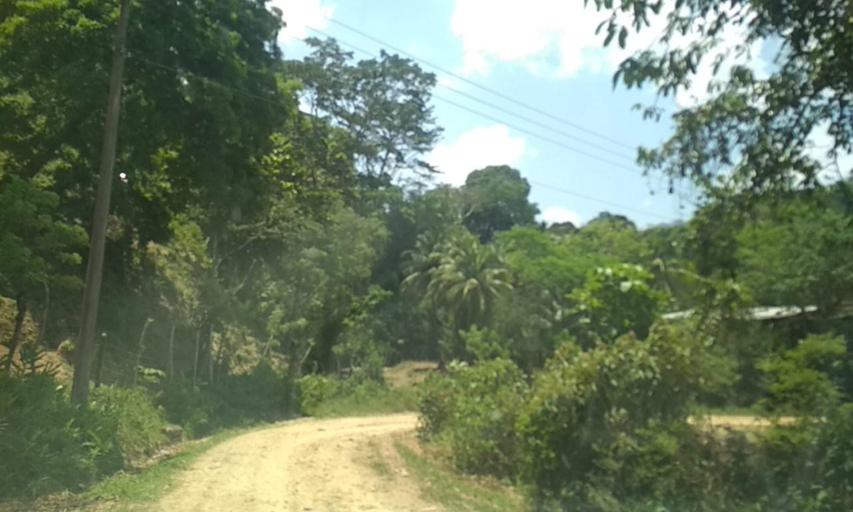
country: MX
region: Chiapas
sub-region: Tecpatan
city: Raudales Malpaso
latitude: 17.3914
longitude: -93.7335
